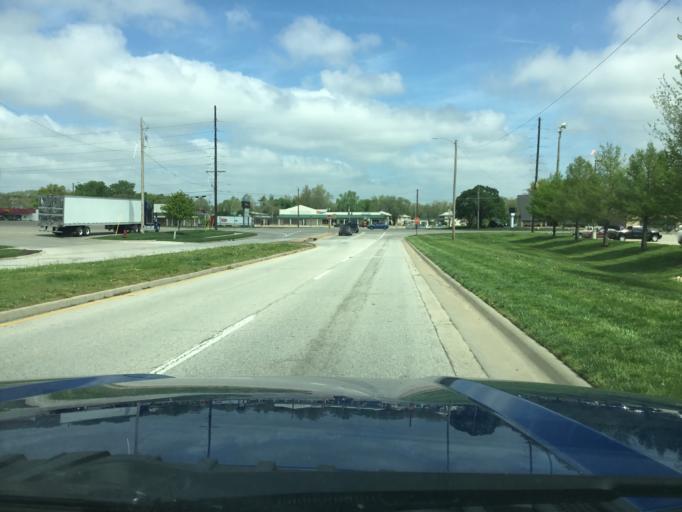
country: US
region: Kansas
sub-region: Shawnee County
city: Topeka
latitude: 39.0431
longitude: -95.6350
